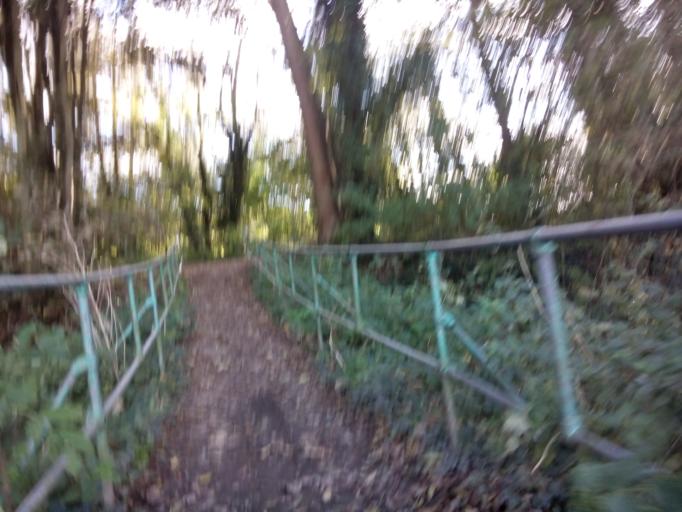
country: GB
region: England
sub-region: Suffolk
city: Sudbury
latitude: 52.0338
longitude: 0.7276
